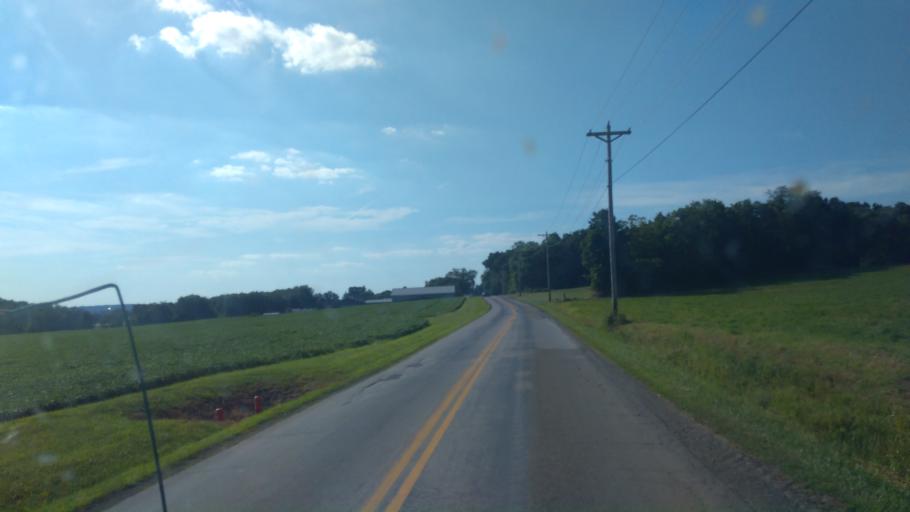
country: US
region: Ohio
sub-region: Wayne County
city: Shreve
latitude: 40.7306
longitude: -82.0572
